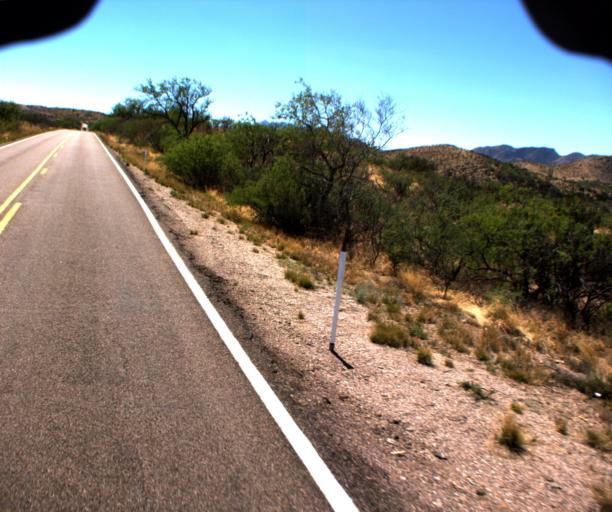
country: US
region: Arizona
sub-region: Pima County
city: Corona de Tucson
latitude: 31.8584
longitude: -110.6938
